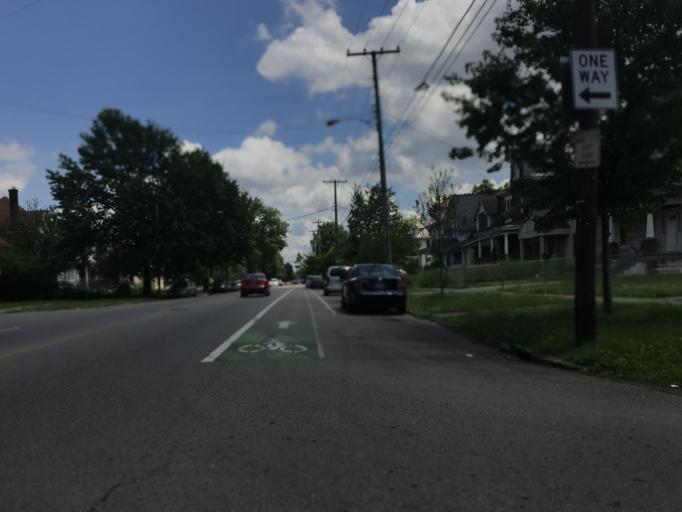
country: US
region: Indiana
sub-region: Floyd County
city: New Albany
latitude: 38.2500
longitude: -85.8139
